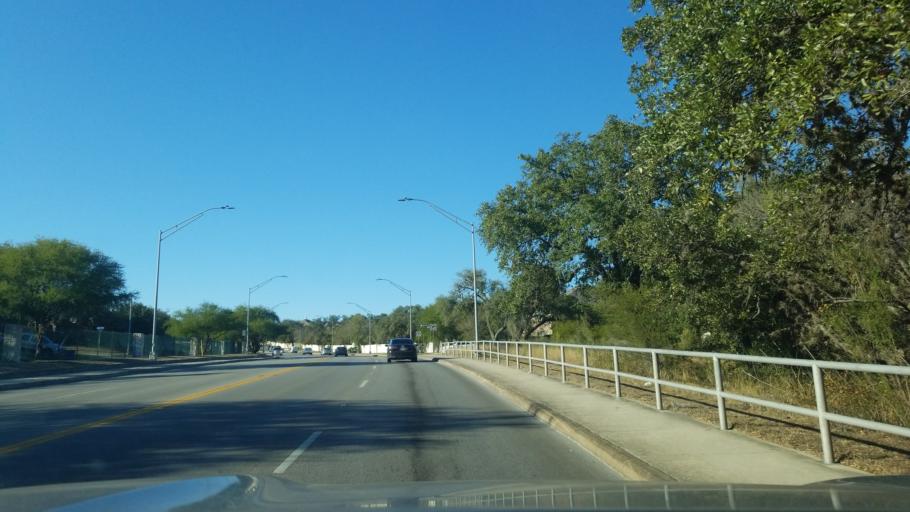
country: US
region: Texas
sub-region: Bexar County
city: Hollywood Park
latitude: 29.6334
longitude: -98.4818
